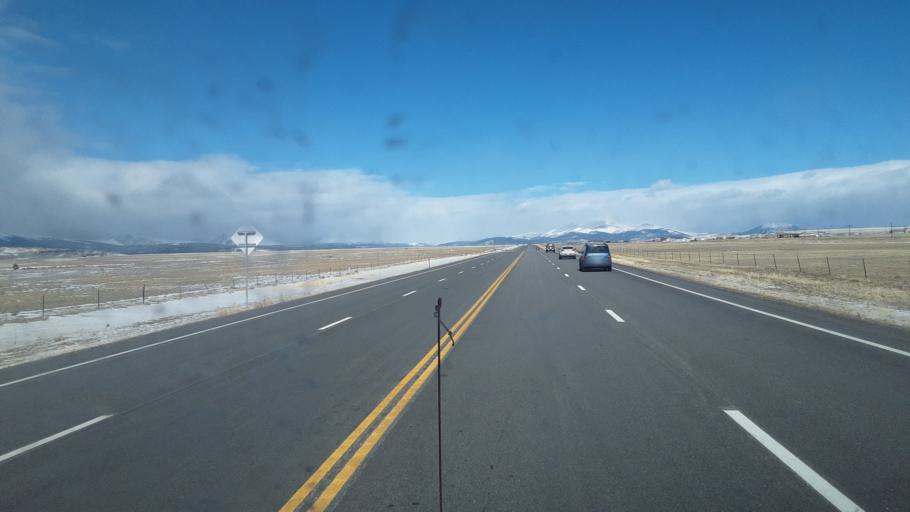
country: US
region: Colorado
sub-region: Park County
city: Fairplay
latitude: 39.1114
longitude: -105.9916
